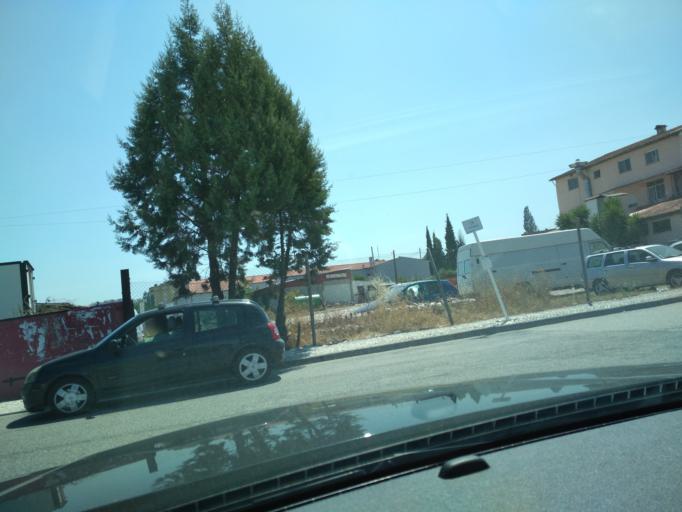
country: PT
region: Coimbra
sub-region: Condeixa-A-Nova
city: Condeixa-a-Nova
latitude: 40.1102
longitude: -8.5074
